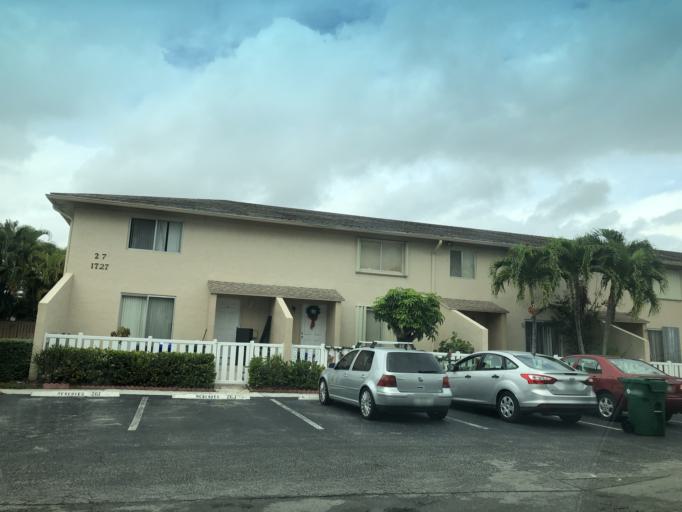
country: US
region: Florida
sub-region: Broward County
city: Margate
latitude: 26.2500
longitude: -80.2334
